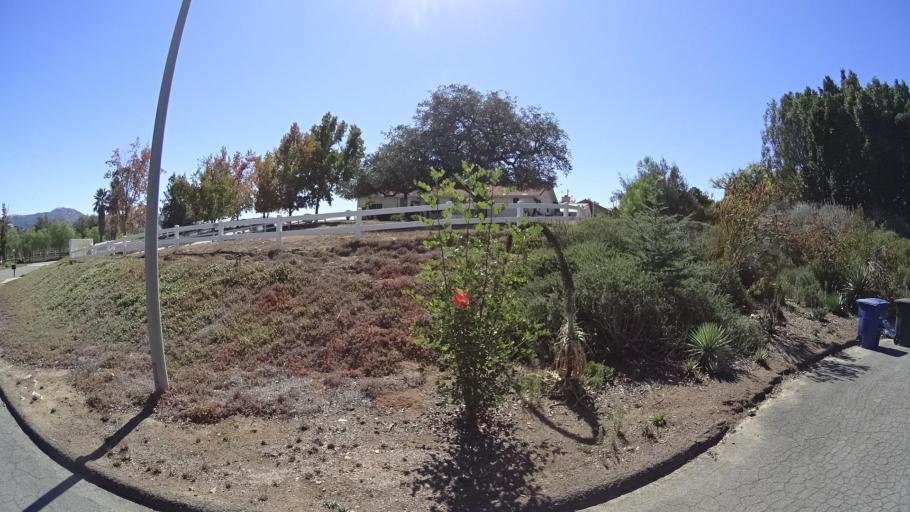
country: US
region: California
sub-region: San Diego County
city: Alpine
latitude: 32.8147
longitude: -116.7821
